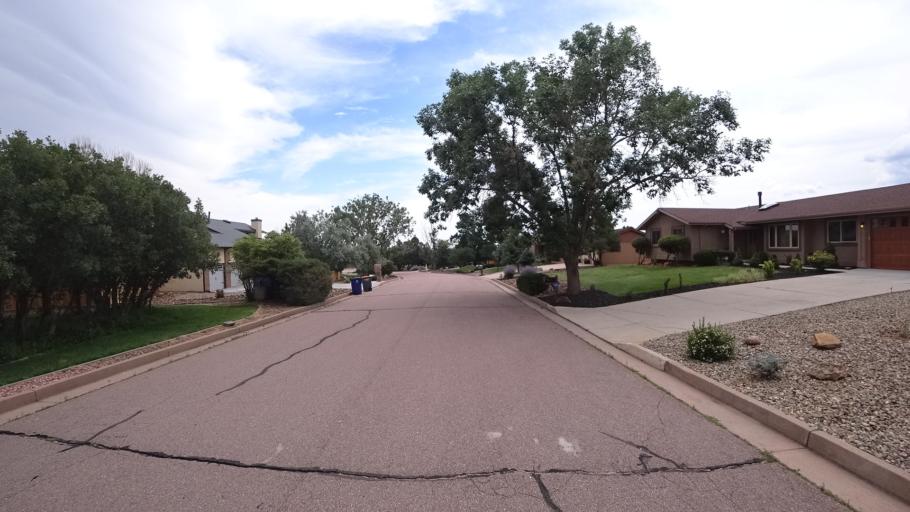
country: US
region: Colorado
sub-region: El Paso County
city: Colorado Springs
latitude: 38.9034
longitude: -104.8334
